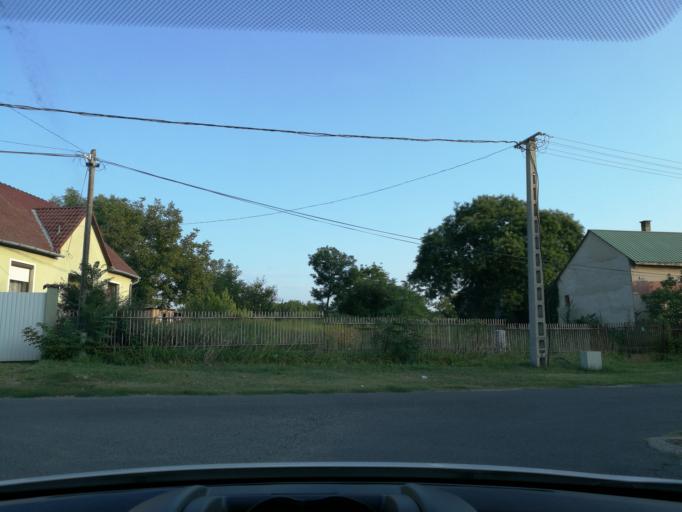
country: HU
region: Szabolcs-Szatmar-Bereg
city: Nyirpazony
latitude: 47.9494
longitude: 21.8009
